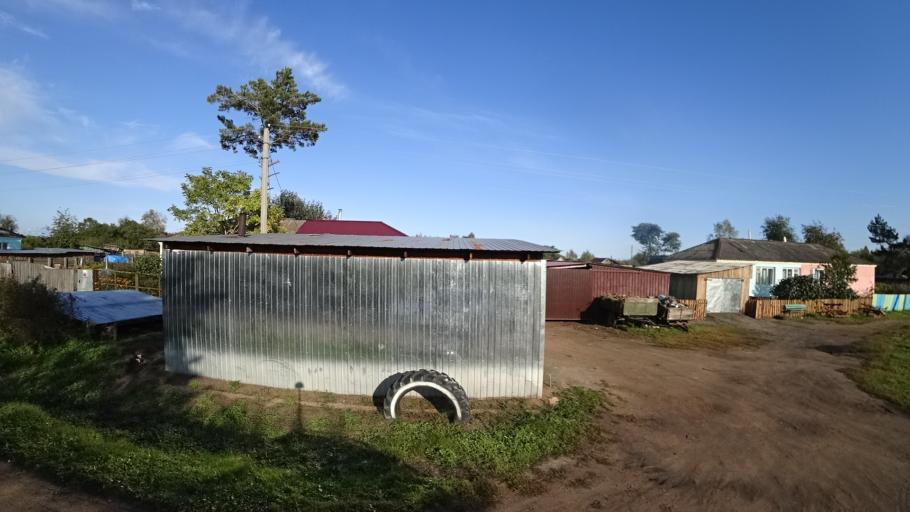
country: RU
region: Amur
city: Arkhara
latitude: 49.3557
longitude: 130.1227
